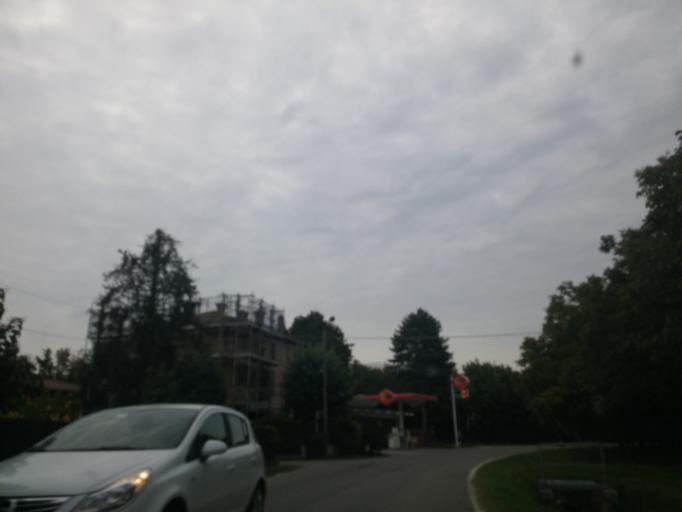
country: IT
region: Emilia-Romagna
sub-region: Provincia di Bologna
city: Trebbo
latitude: 44.5780
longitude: 11.3256
